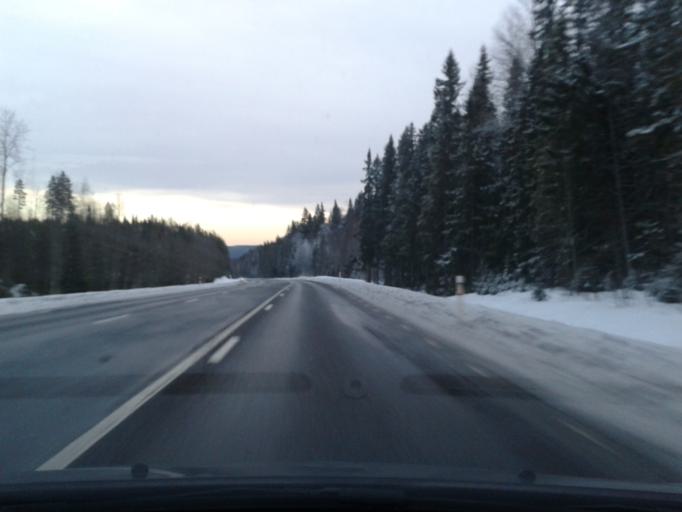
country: SE
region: Vaesternorrland
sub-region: Kramfors Kommun
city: Bollstabruk
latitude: 63.1175
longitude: 17.4925
